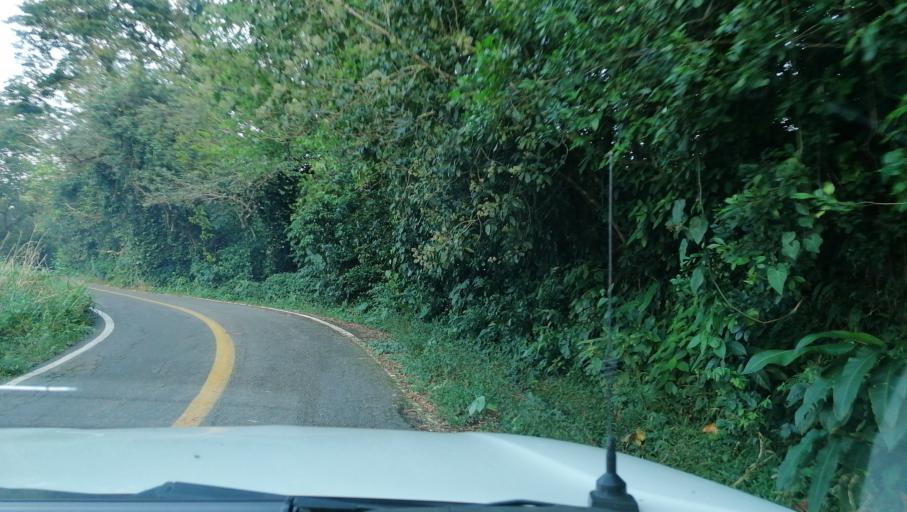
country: MX
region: Chiapas
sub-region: Juarez
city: El Triunfo 1ra. Seccion (Cardona)
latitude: 17.5040
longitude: -93.2364
